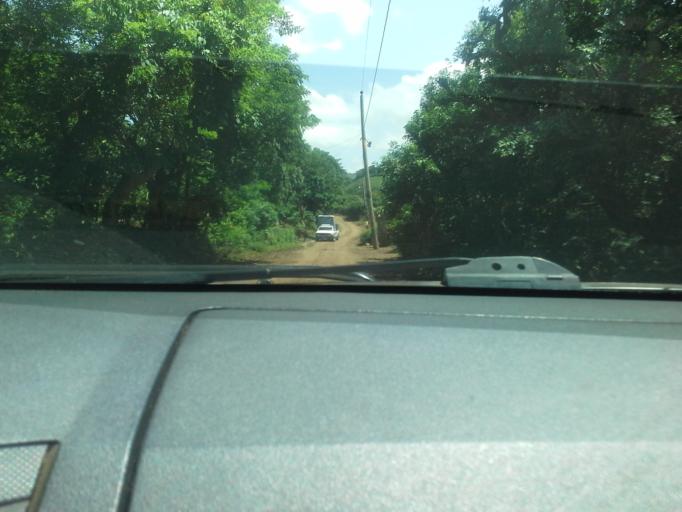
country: NI
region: Matagalpa
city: Terrabona
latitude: 12.7436
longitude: -85.9230
